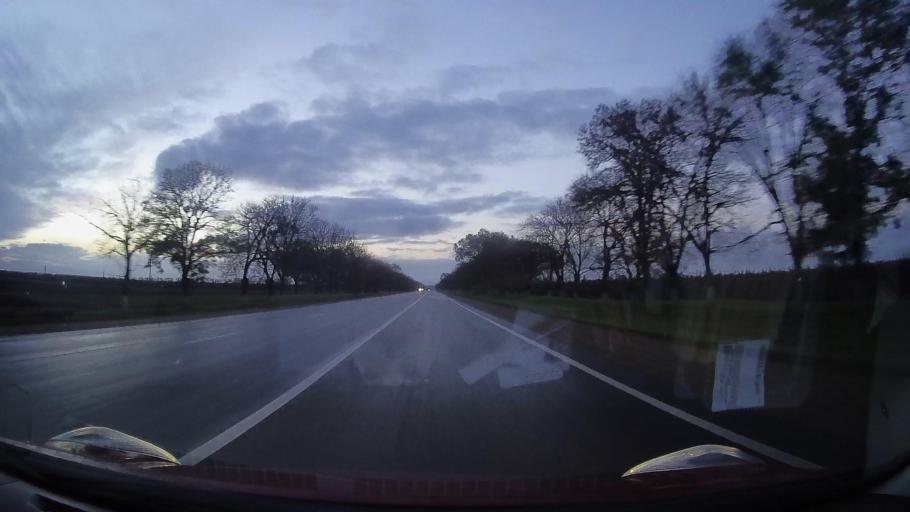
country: RU
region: Krasnodarskiy
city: Zavetnyy
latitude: 44.8993
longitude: 41.1882
